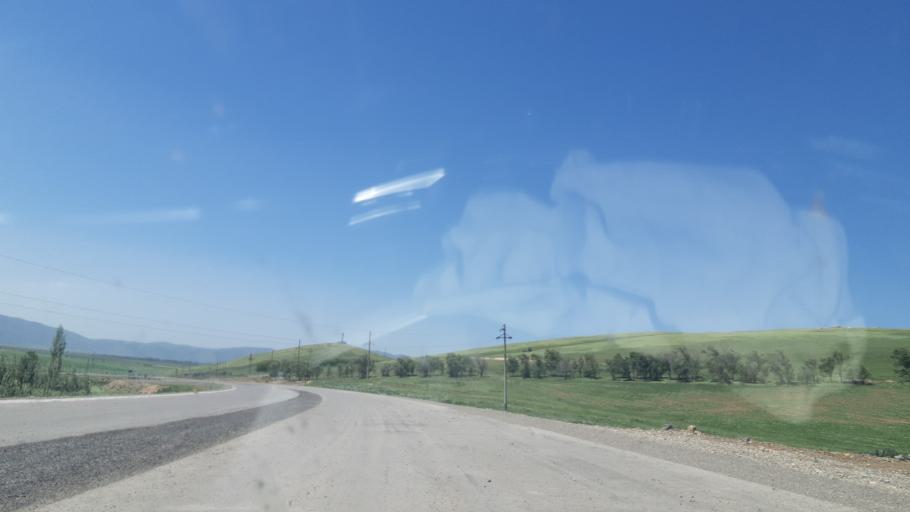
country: KZ
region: Ongtustik Qazaqstan
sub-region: Tulkibas Audany
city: Zhabagly
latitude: 42.5175
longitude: 70.5361
